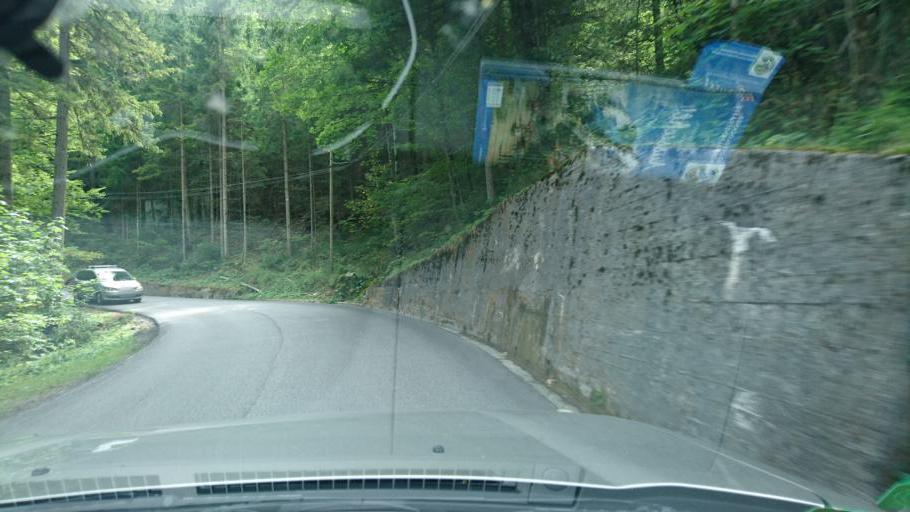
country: AT
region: Carinthia
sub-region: Politischer Bezirk Villach Land
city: Hohenthurn
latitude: 46.4925
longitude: 13.6689
